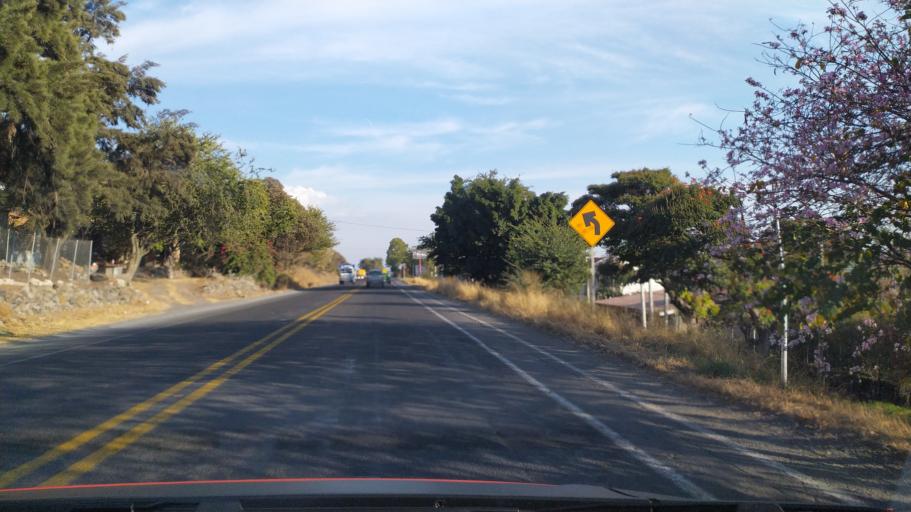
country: MX
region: Jalisco
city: Jamay
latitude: 20.2948
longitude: -102.7542
